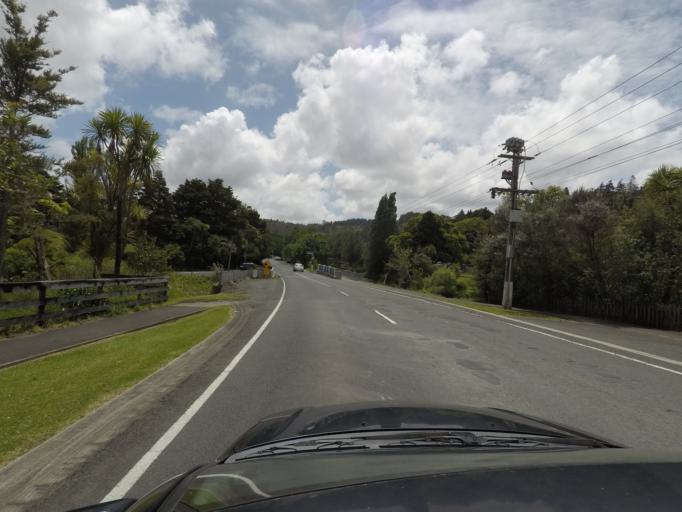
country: NZ
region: Auckland
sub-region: Auckland
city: Warkworth
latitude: -36.5137
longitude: 174.6621
